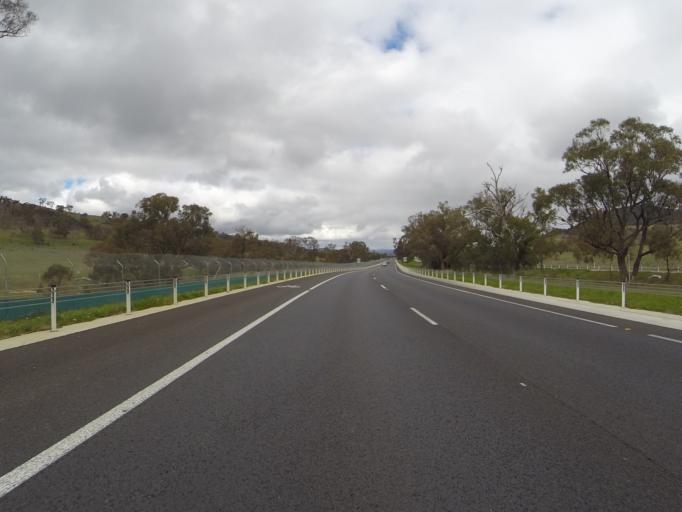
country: AU
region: Australian Capital Territory
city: Kaleen
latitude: -35.2193
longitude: 149.1959
